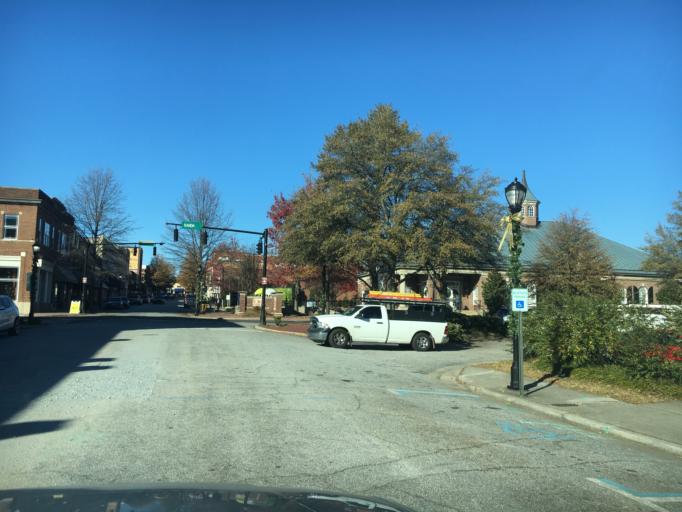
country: US
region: South Carolina
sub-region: Greenville County
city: Greer
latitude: 34.9362
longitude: -82.2260
